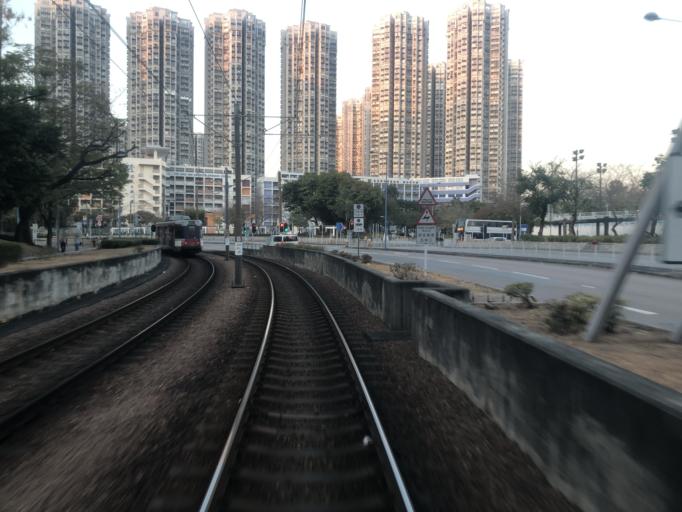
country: HK
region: Yuen Long
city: Yuen Long Kau Hui
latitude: 22.4558
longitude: 114.0060
